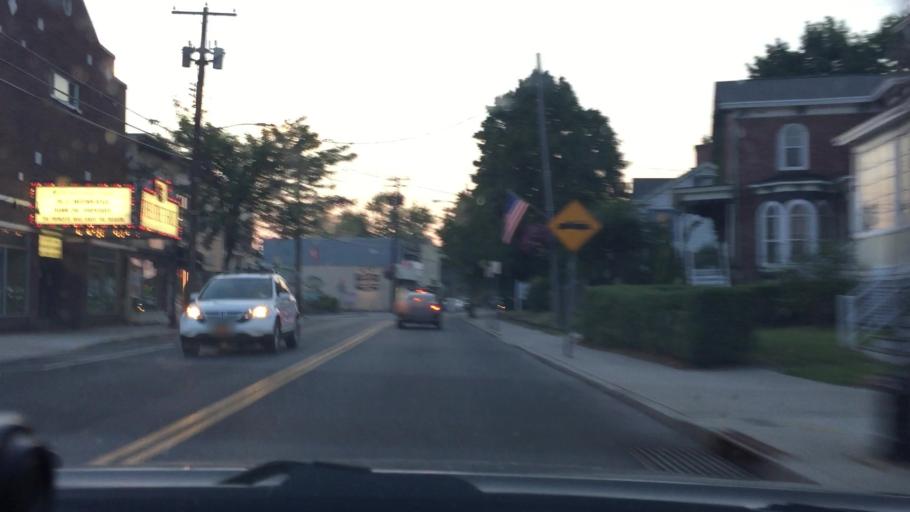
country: US
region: New York
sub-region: Suffolk County
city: Port Jefferson
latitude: 40.9437
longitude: -73.0671
